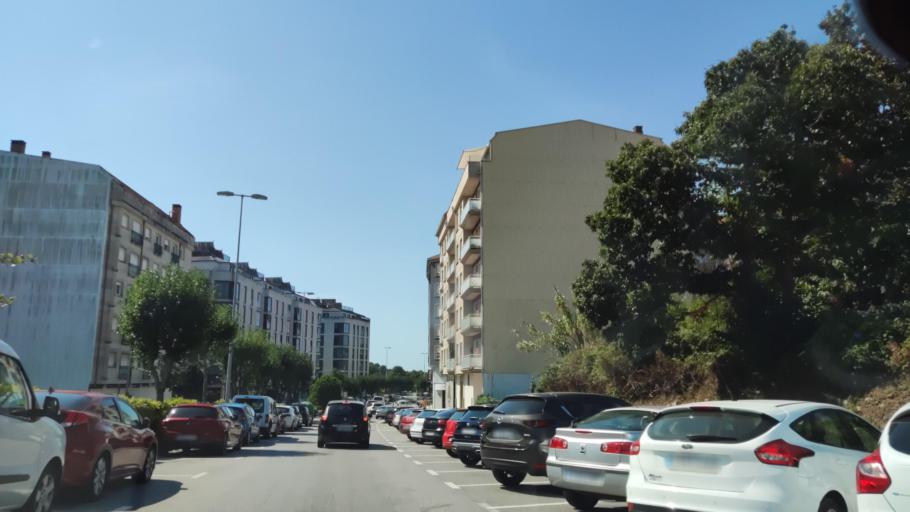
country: ES
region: Galicia
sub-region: Provincia da Coruna
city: Boiro
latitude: 42.6489
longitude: -8.8788
